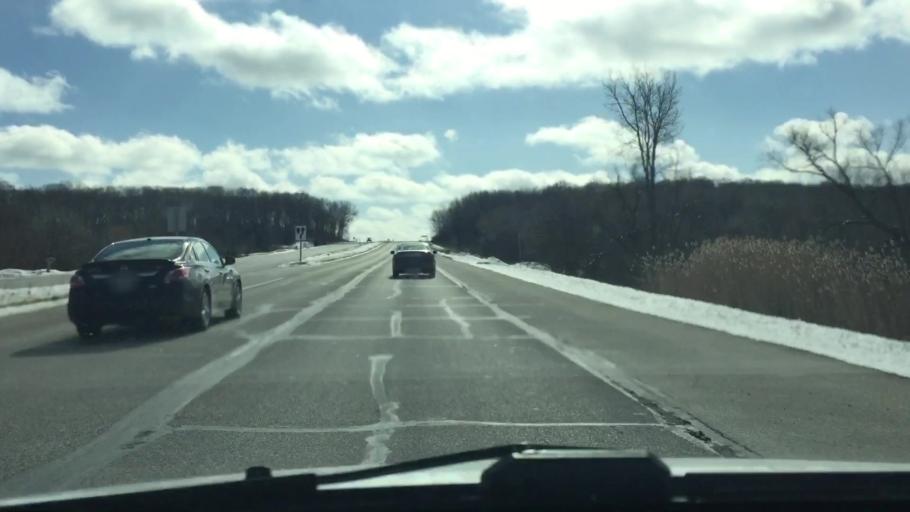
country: US
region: Wisconsin
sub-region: Waukesha County
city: Big Bend
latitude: 42.9416
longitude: -88.2284
